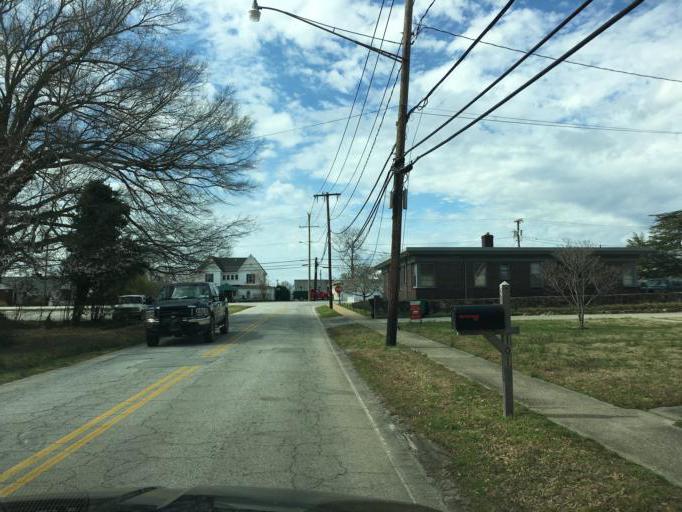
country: US
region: South Carolina
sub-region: Greenville County
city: Fountain Inn
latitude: 34.6931
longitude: -82.1968
